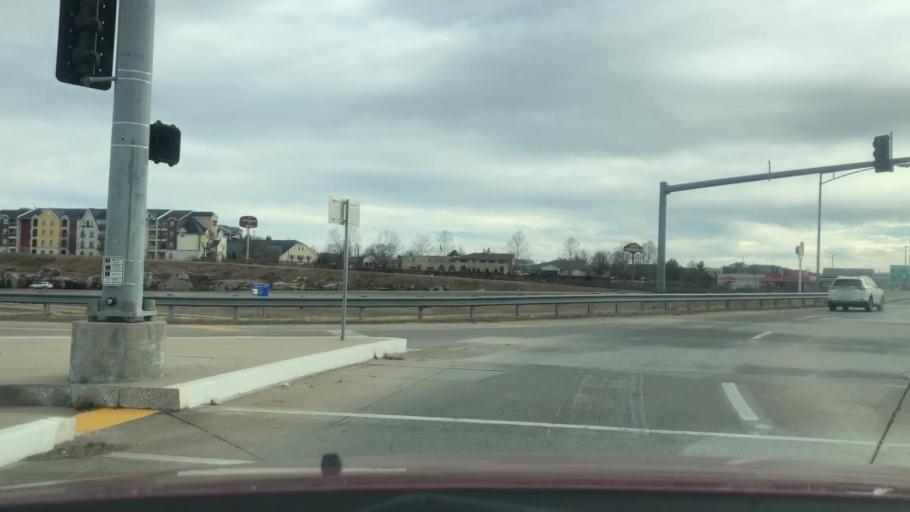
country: US
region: Missouri
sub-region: Greene County
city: Springfield
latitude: 37.1429
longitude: -93.2780
